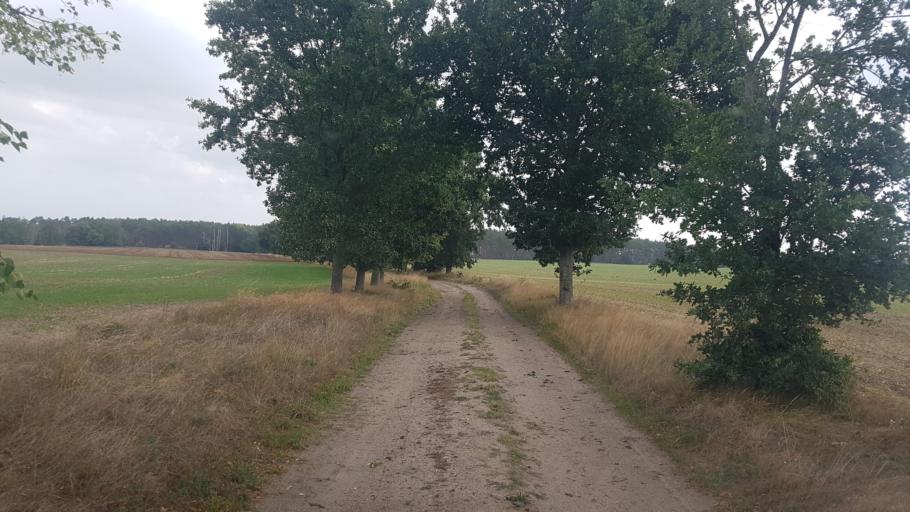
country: DE
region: Brandenburg
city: Belzig
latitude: 52.1634
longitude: 12.6619
